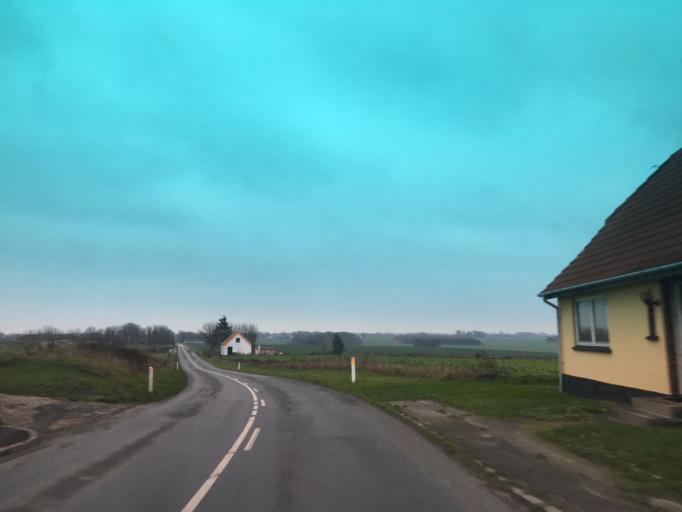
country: DK
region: Zealand
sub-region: Slagelse Kommune
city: Skaelskor
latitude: 55.2822
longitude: 11.3919
